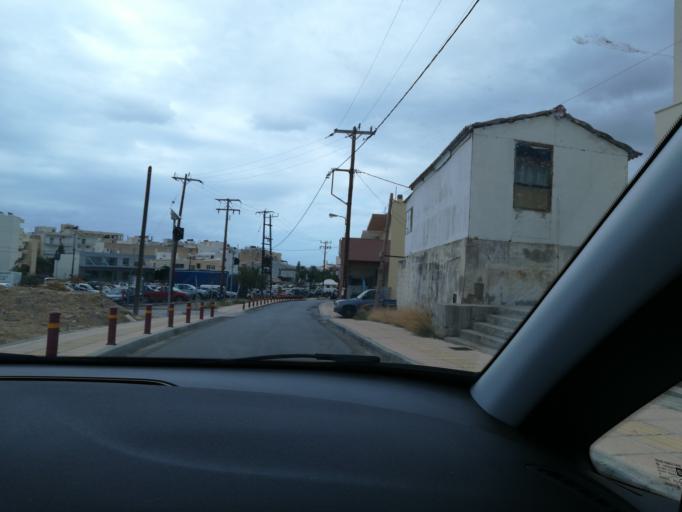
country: GR
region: Crete
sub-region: Nomos Lasithiou
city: Siteia
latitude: 35.2047
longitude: 26.1024
